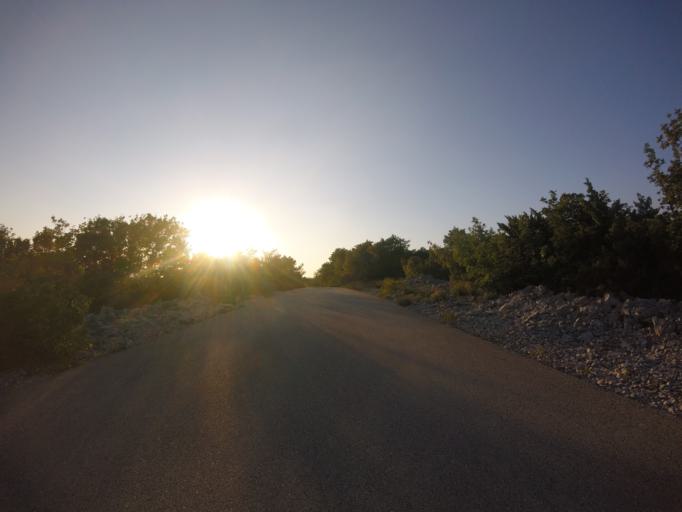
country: HR
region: Primorsko-Goranska
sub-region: Grad Crikvenica
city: Jadranovo
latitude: 45.2112
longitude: 14.6390
